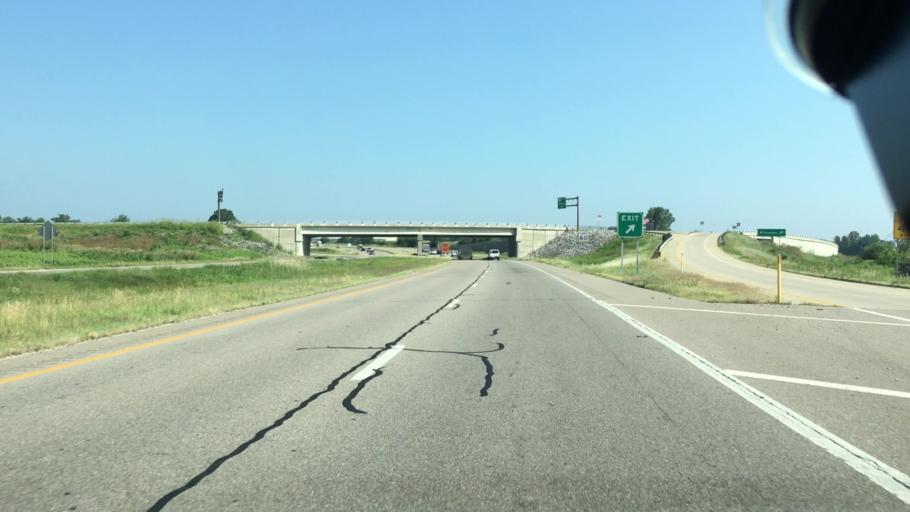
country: US
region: Indiana
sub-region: Gibson County
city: Princeton
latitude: 38.3108
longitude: -87.5678
